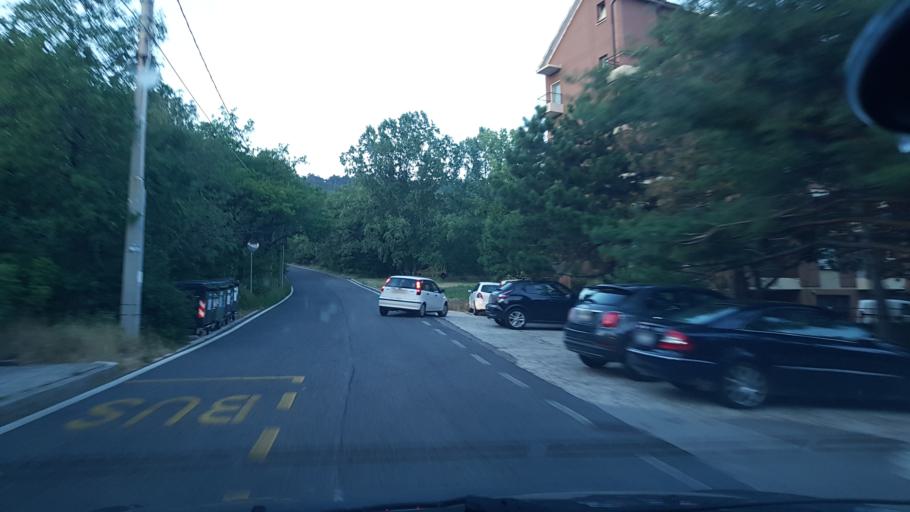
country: IT
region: Friuli Venezia Giulia
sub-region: Provincia di Trieste
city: Villa Opicina
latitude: 45.6772
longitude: 13.7695
